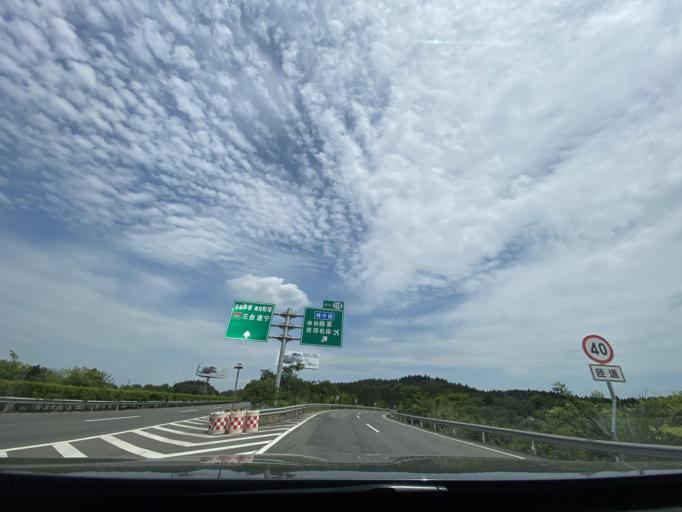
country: CN
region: Sichuan
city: Mianyang
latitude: 31.3512
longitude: 104.7051
